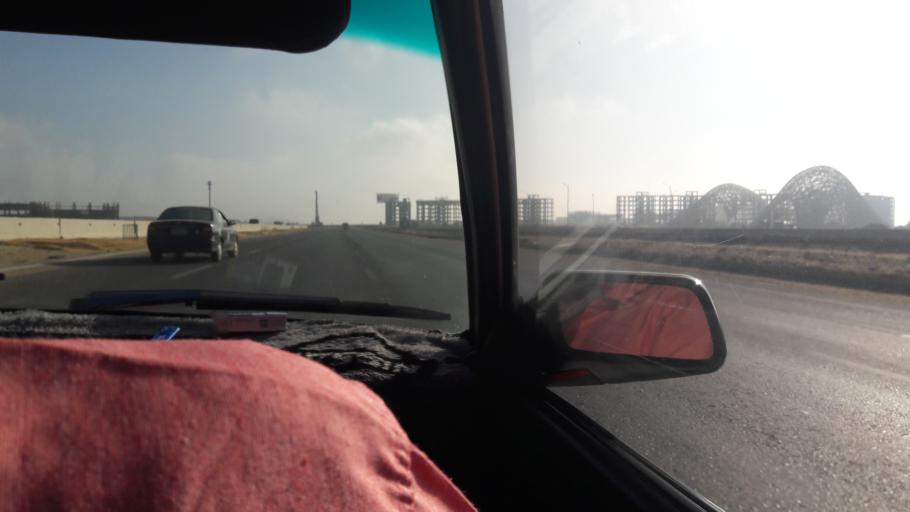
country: EG
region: Muhafazat al Qalyubiyah
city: Al Khankah
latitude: 30.0491
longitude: 31.6099
